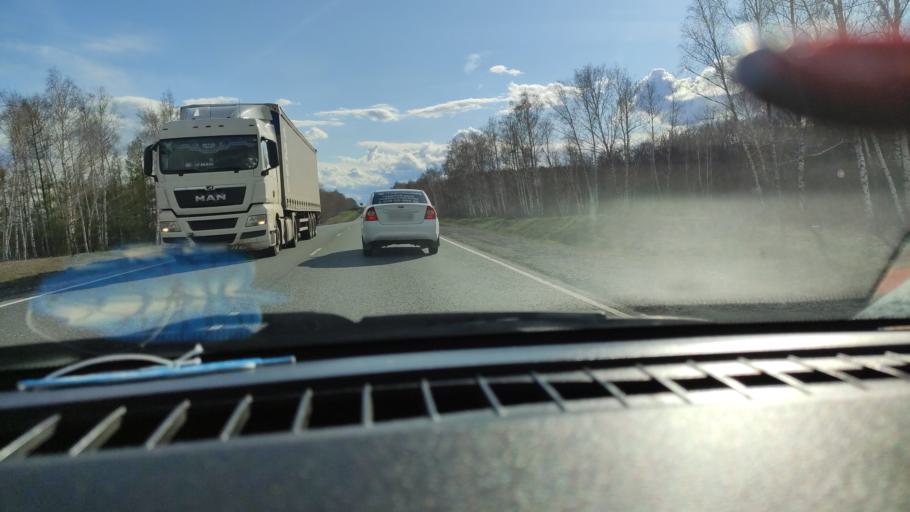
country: RU
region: Saratov
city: Sennoy
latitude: 52.1207
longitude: 46.8454
